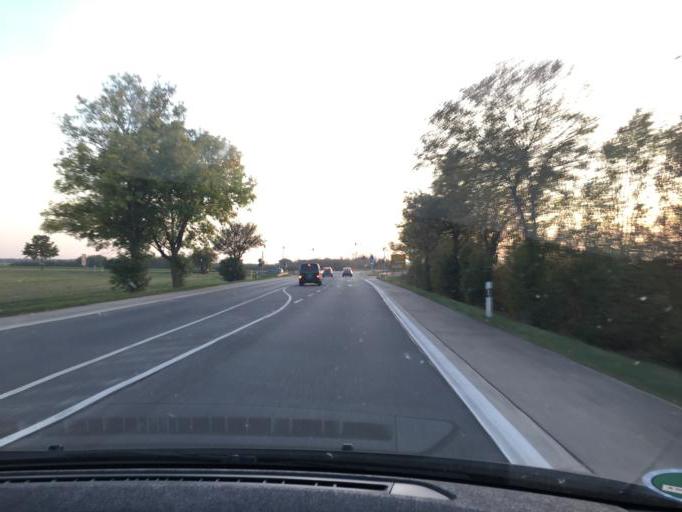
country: DE
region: North Rhine-Westphalia
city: Tuernich
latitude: 50.8325
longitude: 6.7555
